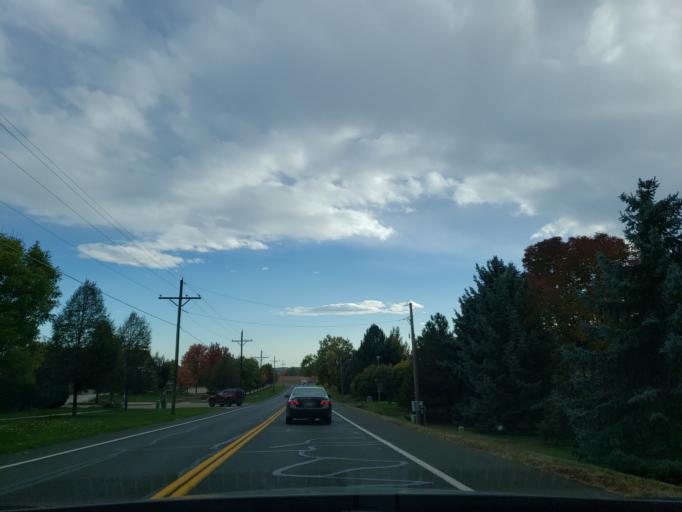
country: US
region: Colorado
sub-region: Larimer County
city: Fort Collins
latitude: 40.6127
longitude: -105.0386
